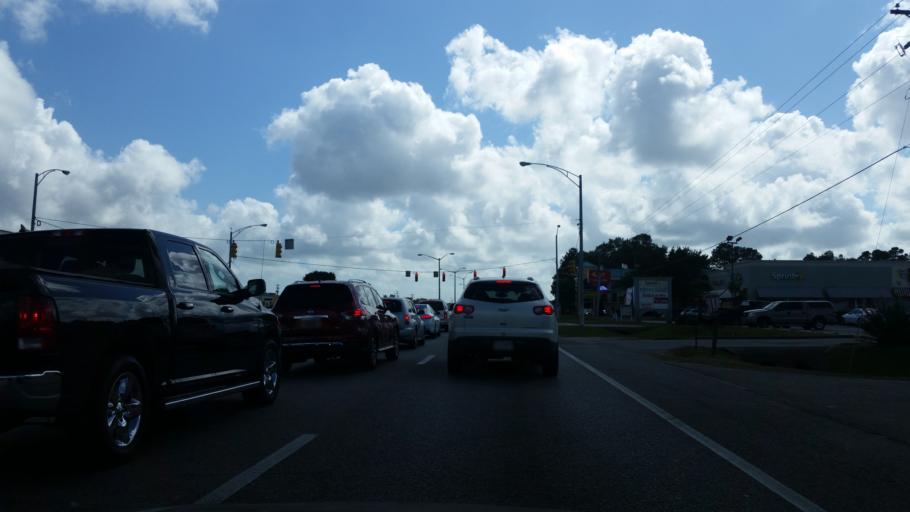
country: US
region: Alabama
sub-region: Baldwin County
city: Foley
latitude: 30.3768
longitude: -87.6834
